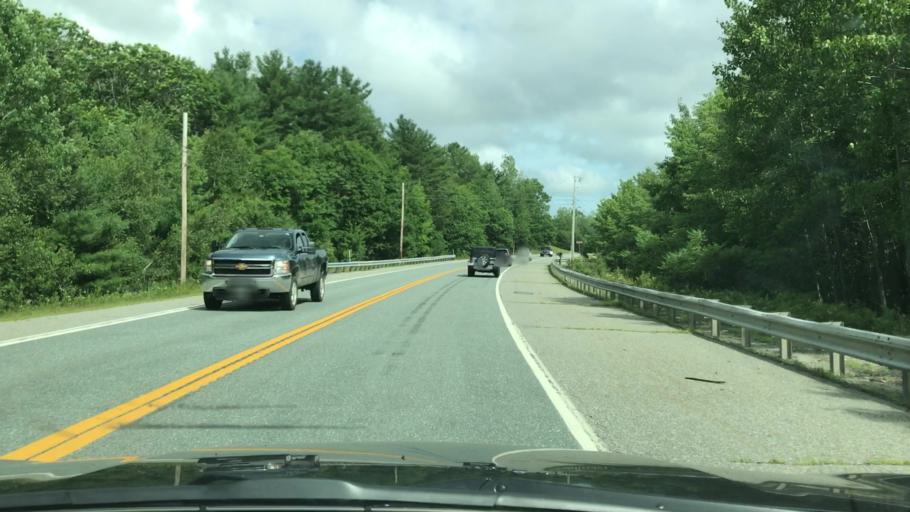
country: US
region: Maine
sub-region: Hancock County
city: Surry
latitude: 44.5634
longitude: -68.5898
